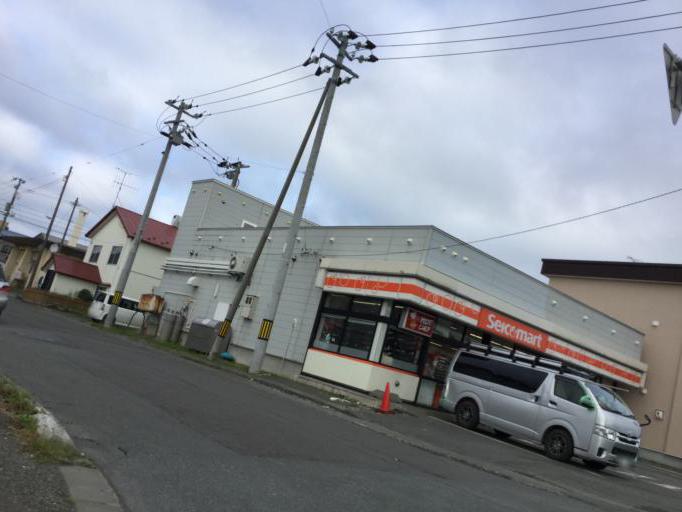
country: JP
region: Hokkaido
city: Wakkanai
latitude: 45.4020
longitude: 141.6792
